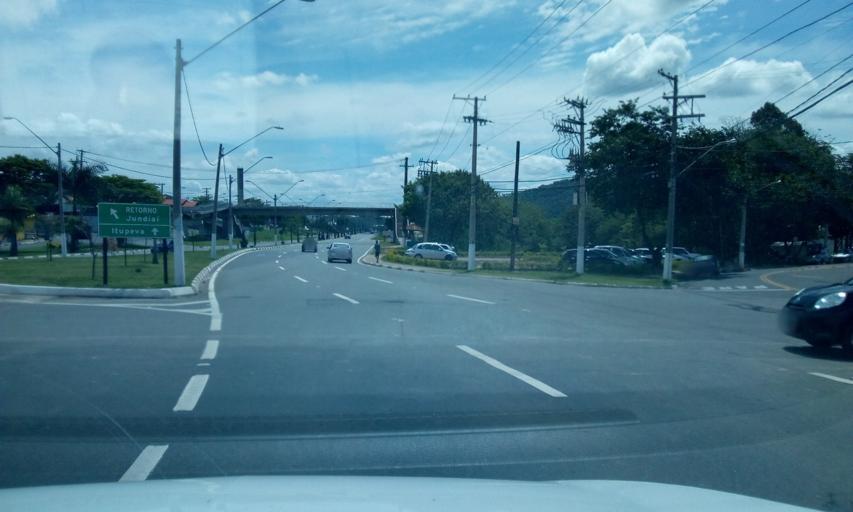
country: BR
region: Sao Paulo
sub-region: Itupeva
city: Itupeva
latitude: -23.1570
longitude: -47.0408
